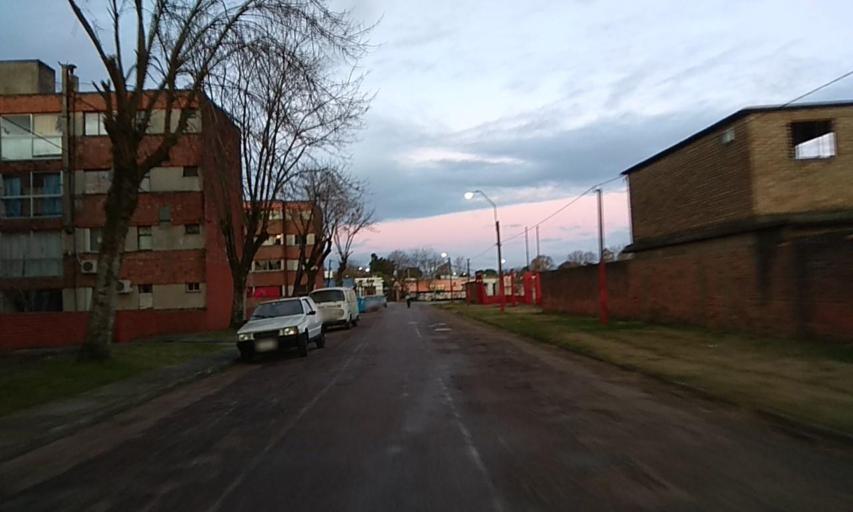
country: UY
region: Florida
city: Florida
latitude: -34.1085
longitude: -56.2140
